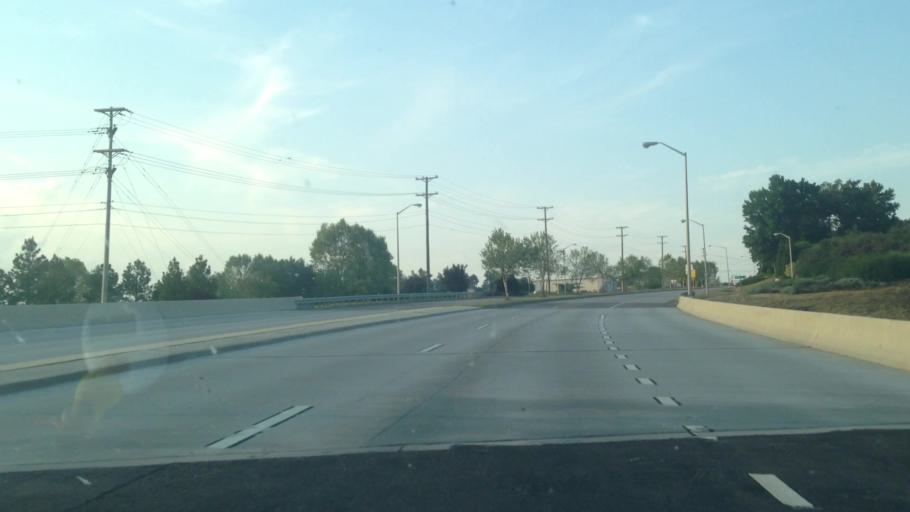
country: US
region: Virginia
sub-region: City of Danville
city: Danville
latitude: 36.5974
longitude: -79.4181
